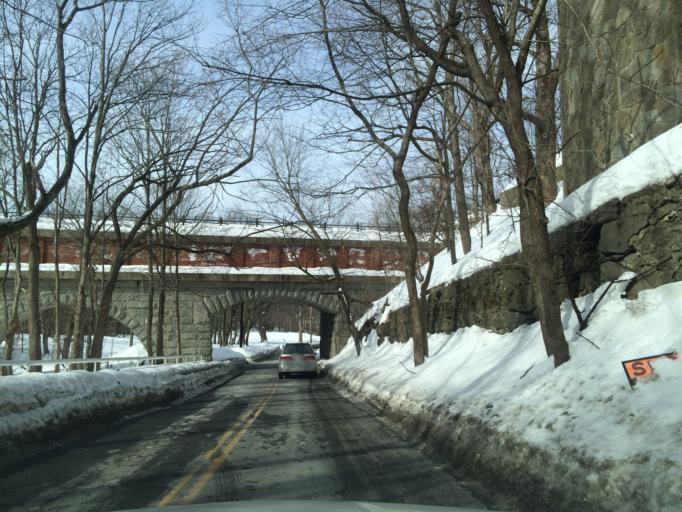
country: US
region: Massachusetts
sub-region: Middlesex County
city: Newton
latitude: 42.3149
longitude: -71.2259
